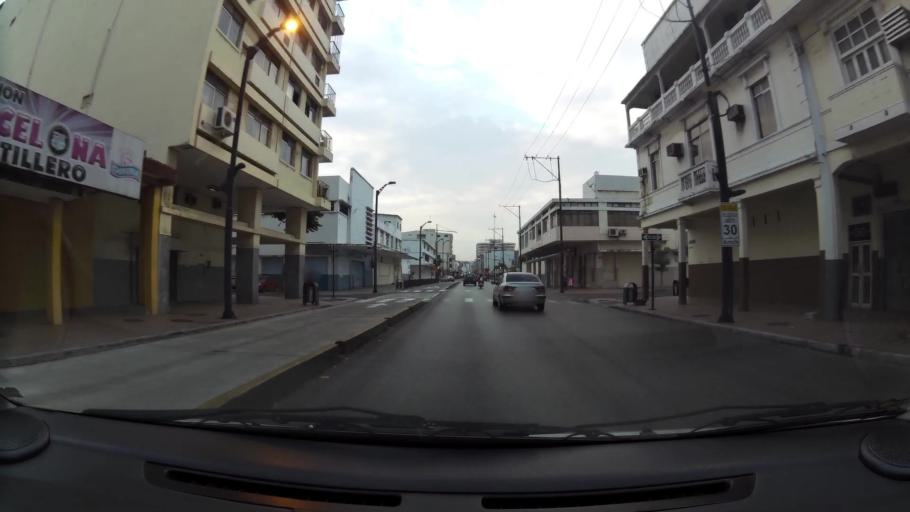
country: EC
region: Guayas
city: Guayaquil
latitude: -2.2076
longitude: -79.8854
